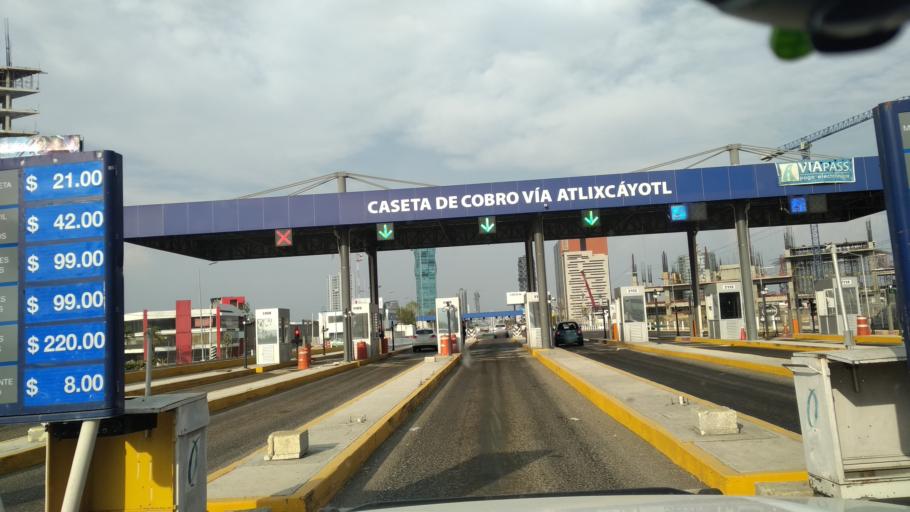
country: MX
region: Puebla
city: Tlazcalancingo
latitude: 19.0038
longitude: -98.2730
